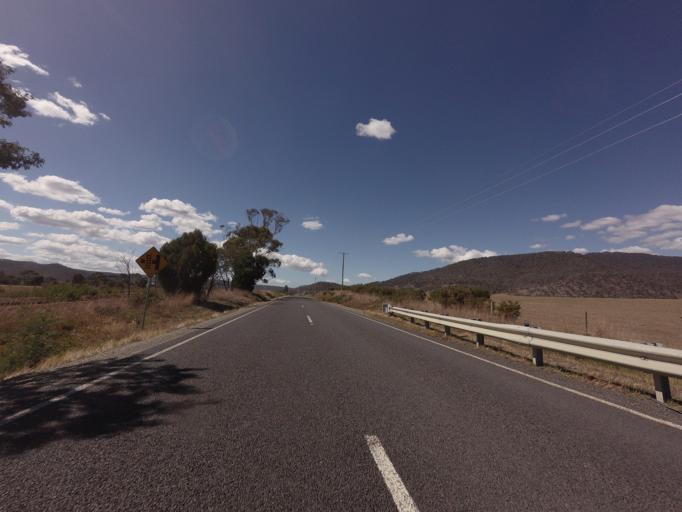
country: AU
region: Tasmania
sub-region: Break O'Day
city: St Helens
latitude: -41.6763
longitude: 147.8947
